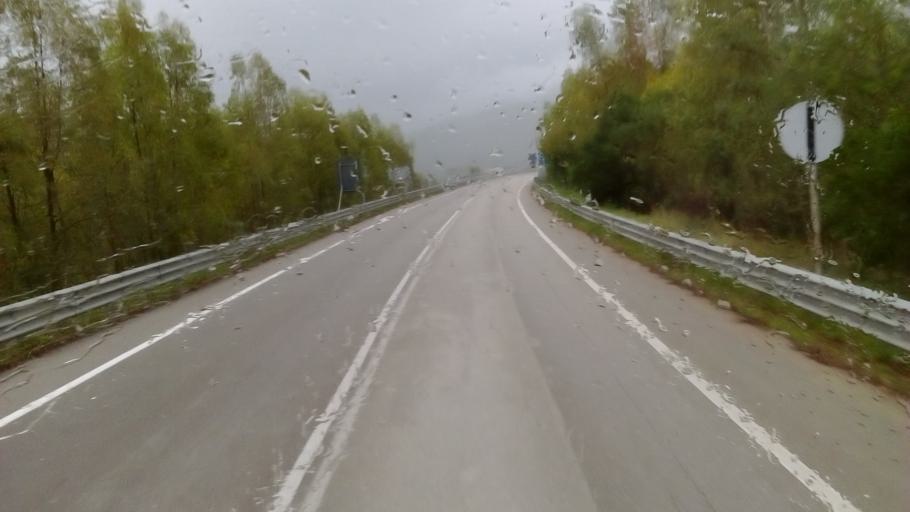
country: IT
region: Sicily
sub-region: Enna
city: Villarosa
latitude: 37.5340
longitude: 14.1298
